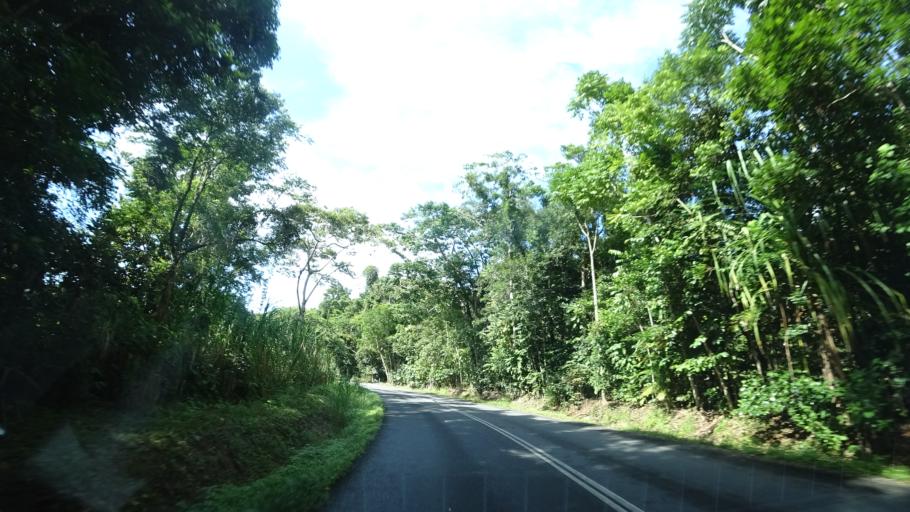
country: AU
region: Queensland
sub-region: Cairns
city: Port Douglas
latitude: -16.1417
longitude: 145.4307
